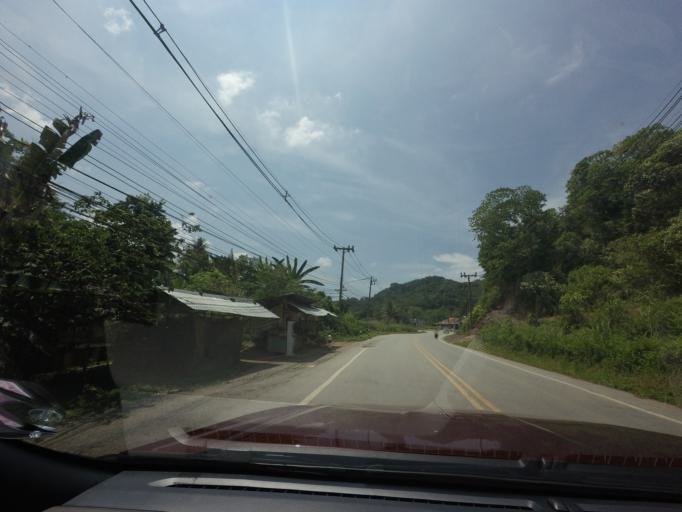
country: TH
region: Yala
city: Betong
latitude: 5.8092
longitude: 101.0815
